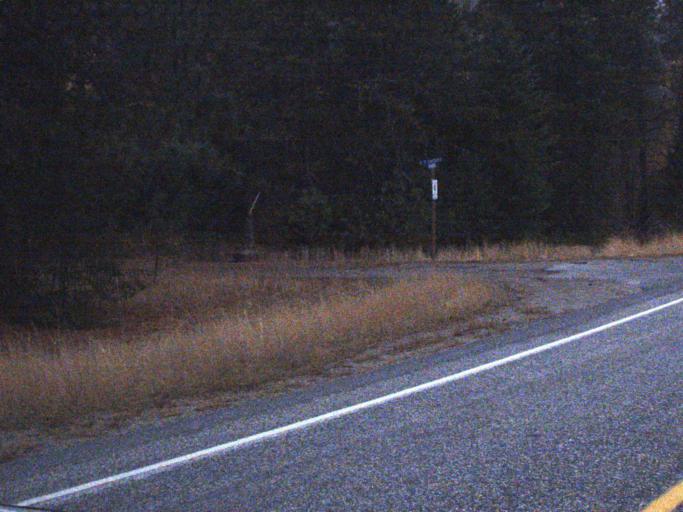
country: US
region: Washington
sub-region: Stevens County
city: Kettle Falls
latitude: 48.7072
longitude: -118.1252
